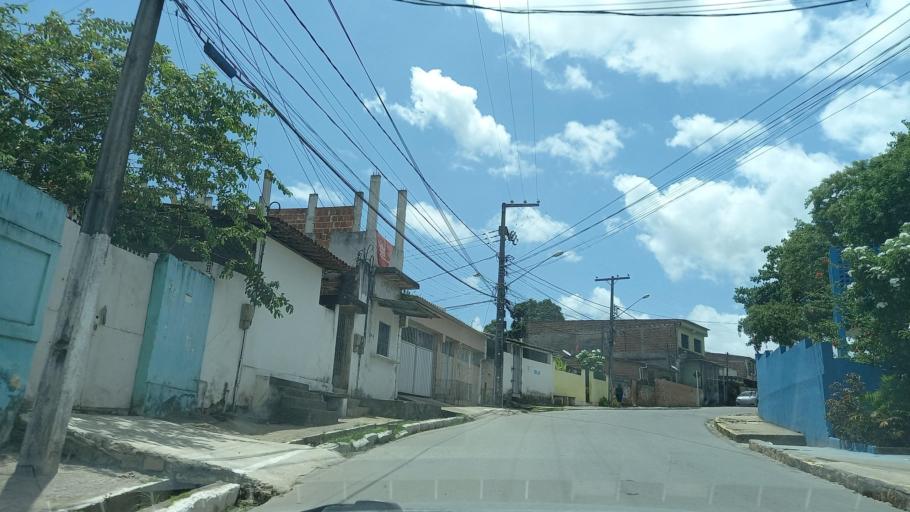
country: BR
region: Pernambuco
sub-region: Jaboatao Dos Guararapes
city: Jaboatao
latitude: -8.1705
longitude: -34.9983
